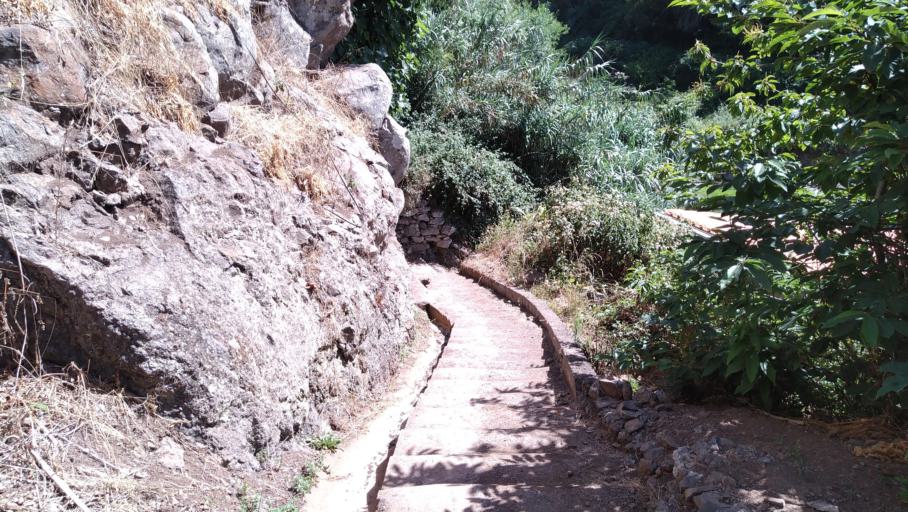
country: PT
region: Madeira
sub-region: Funchal
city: Nossa Senhora do Monte
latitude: 32.6812
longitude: -16.9408
